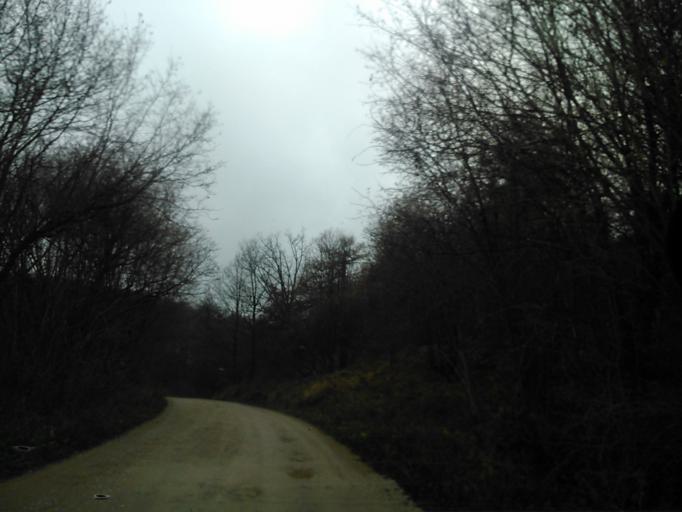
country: PL
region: Kujawsko-Pomorskie
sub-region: Powiat golubsko-dobrzynski
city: Radomin
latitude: 53.1275
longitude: 19.1693
